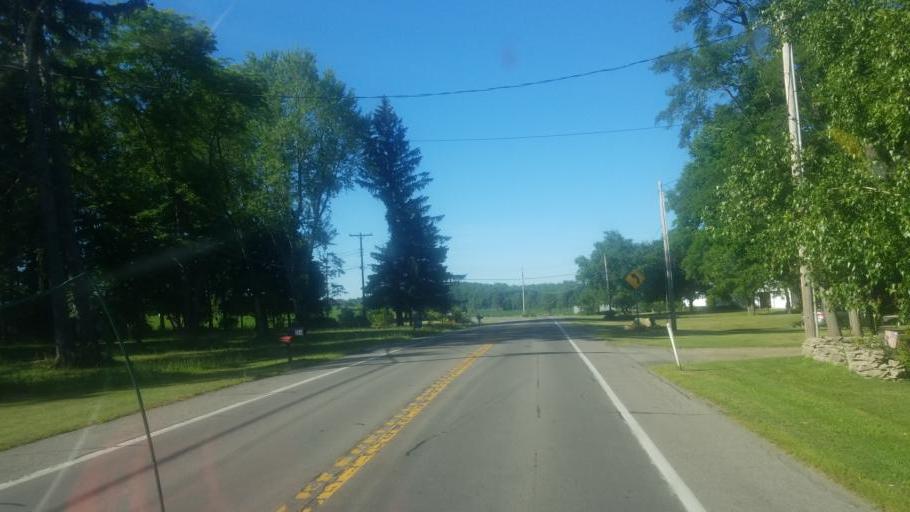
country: US
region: New York
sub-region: Wayne County
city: Newark
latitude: 43.0073
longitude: -77.0940
